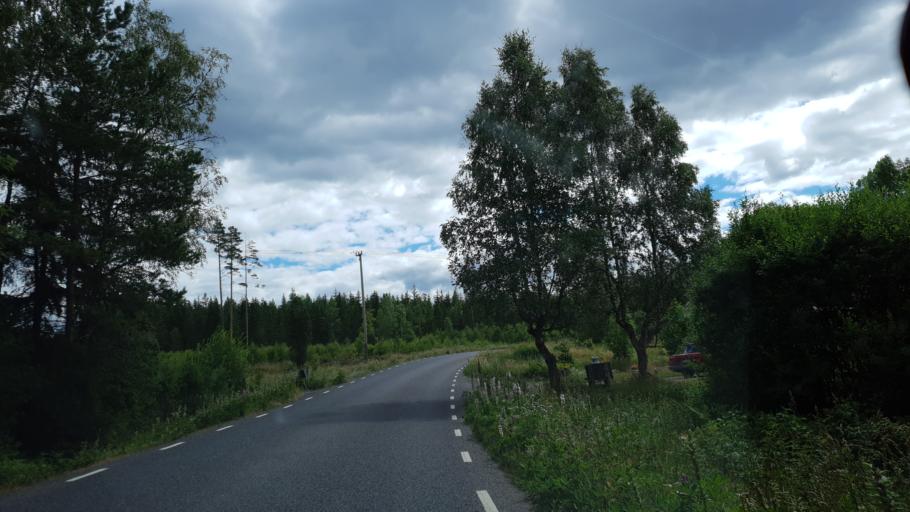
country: SE
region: Kronoberg
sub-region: Uppvidinge Kommun
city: Aseda
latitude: 57.1918
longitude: 15.3992
